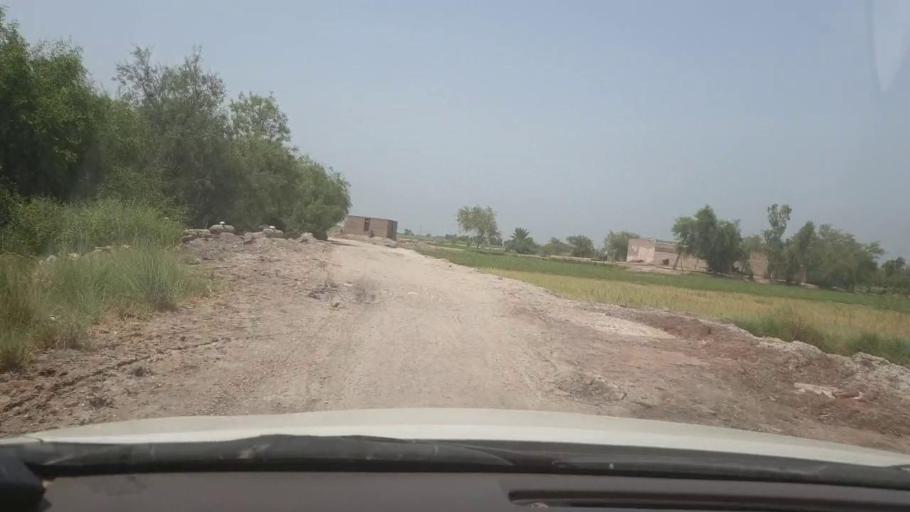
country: PK
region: Sindh
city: Shikarpur
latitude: 27.9574
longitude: 68.5940
